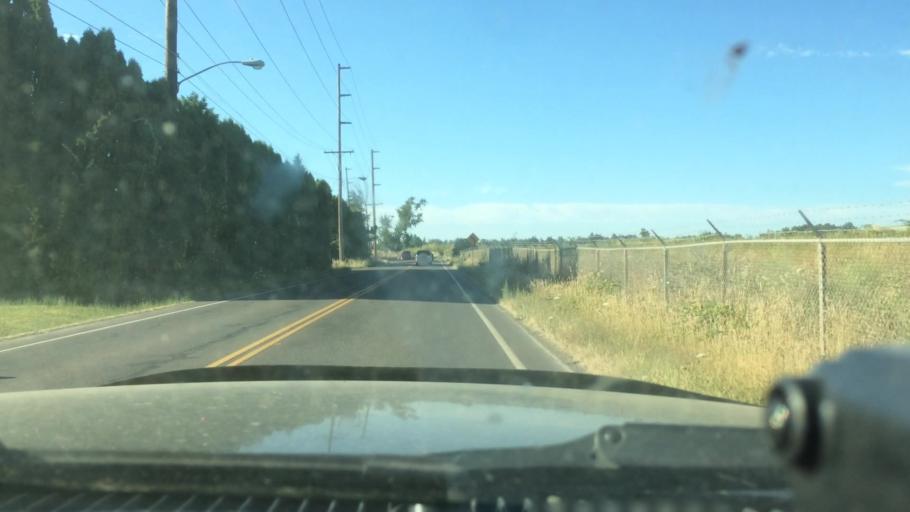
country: US
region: Oregon
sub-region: Lane County
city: Eugene
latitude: 44.0995
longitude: -123.1142
